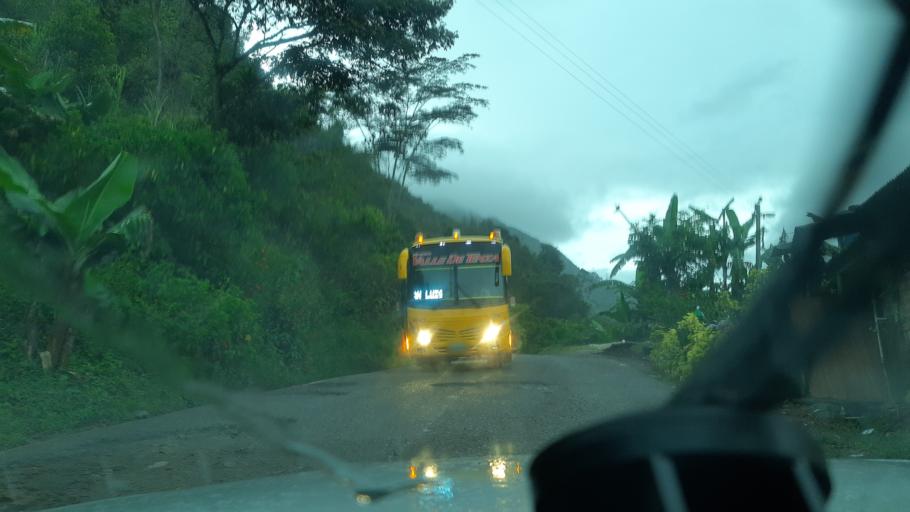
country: CO
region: Boyaca
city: Chinavita
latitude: 5.1976
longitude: -73.3827
